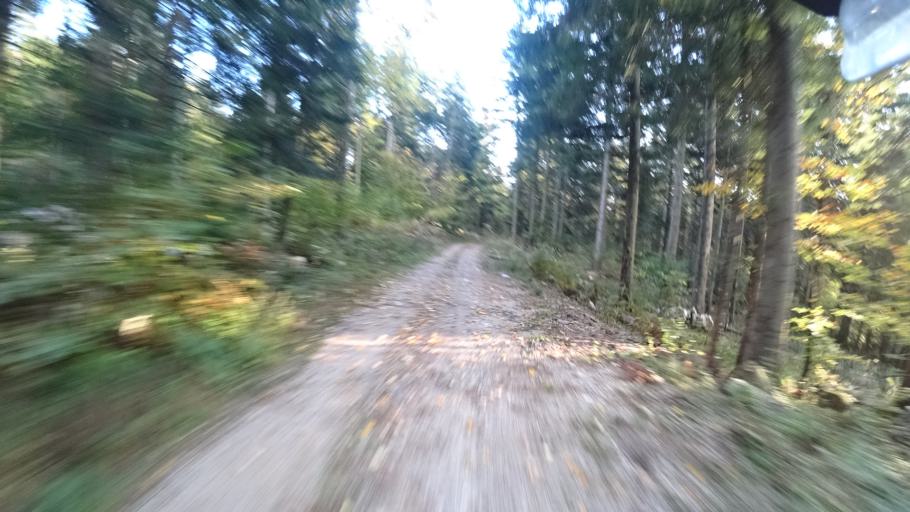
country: HR
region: Karlovacka
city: Plaski
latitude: 45.0202
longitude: 15.4337
